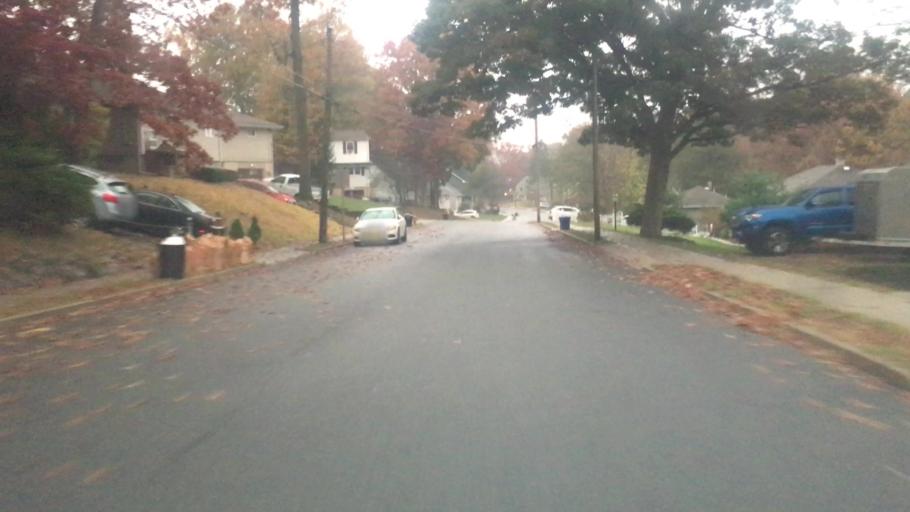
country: US
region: New Jersey
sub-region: Passaic County
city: Bloomingdale
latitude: 41.0123
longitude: -74.3266
